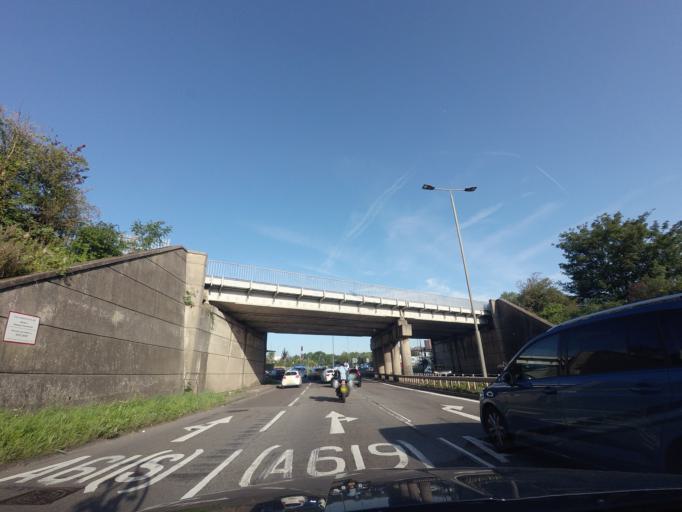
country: GB
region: England
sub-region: Derbyshire
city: Chesterfield
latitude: 53.2305
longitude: -1.4211
